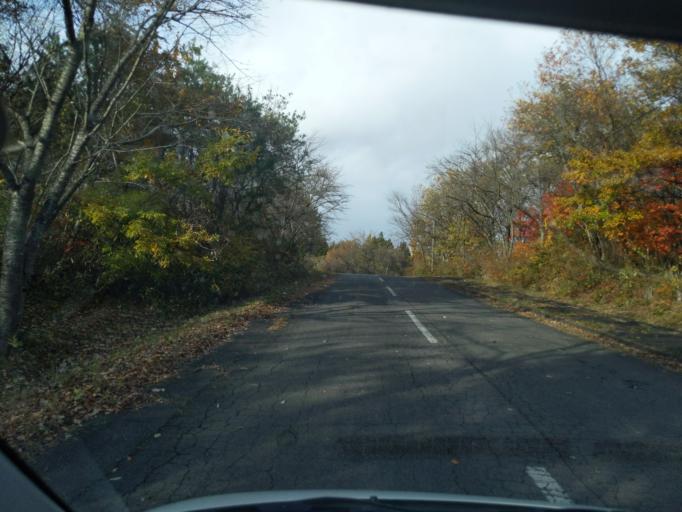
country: JP
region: Iwate
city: Mizusawa
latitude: 39.0276
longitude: 141.0930
